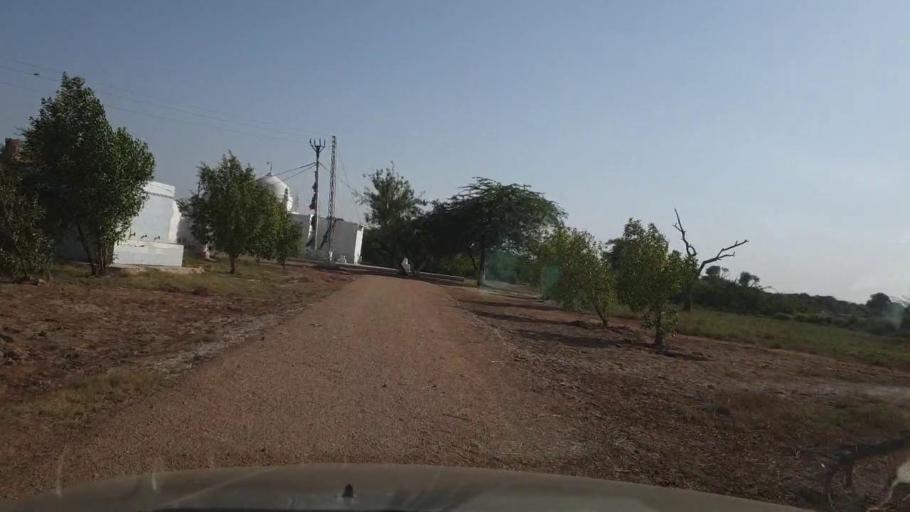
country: PK
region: Sindh
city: Daro Mehar
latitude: 24.9871
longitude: 68.1487
